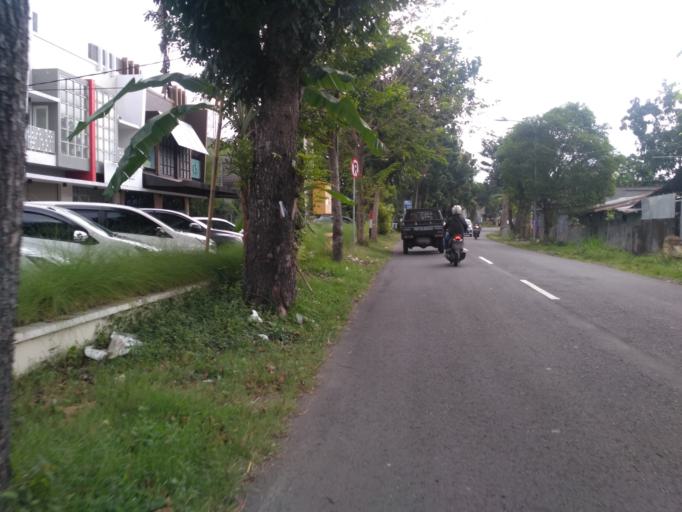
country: ID
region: Daerah Istimewa Yogyakarta
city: Melati
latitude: -7.7403
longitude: 110.3584
